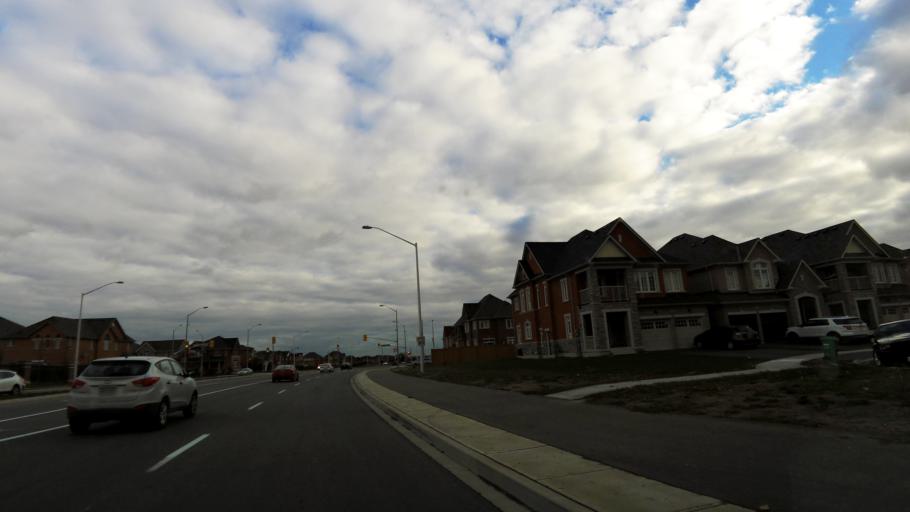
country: CA
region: Ontario
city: Brampton
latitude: 43.7695
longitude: -79.7228
